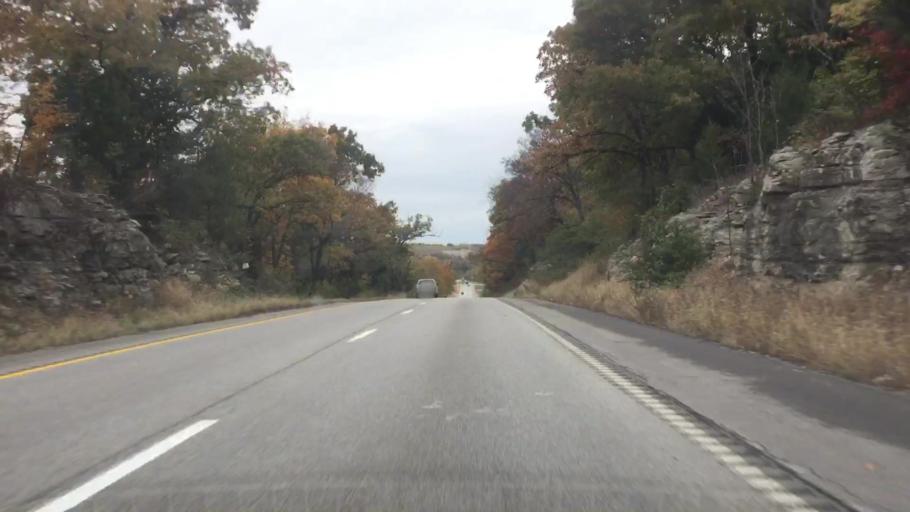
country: US
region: Missouri
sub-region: Jackson County
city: Lees Summit
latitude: 38.9566
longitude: -94.4203
